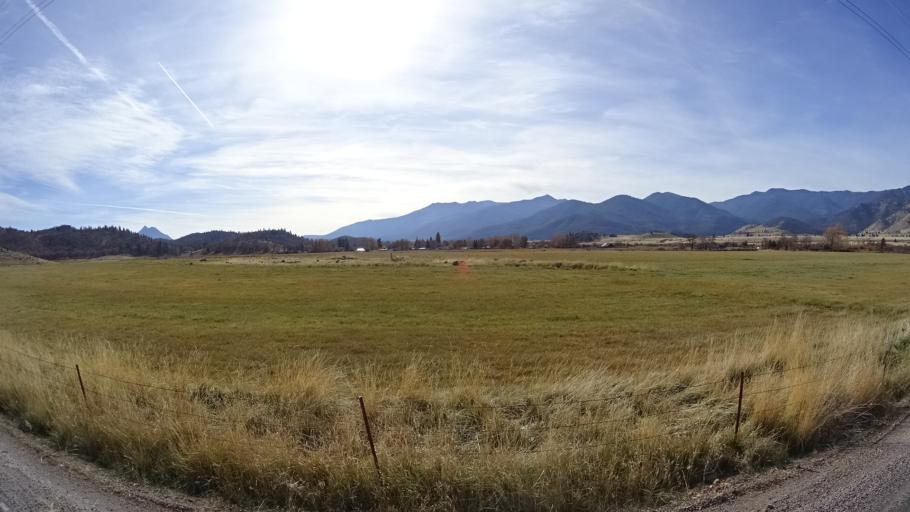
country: US
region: California
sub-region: Siskiyou County
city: Weed
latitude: 41.4675
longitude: -122.4305
